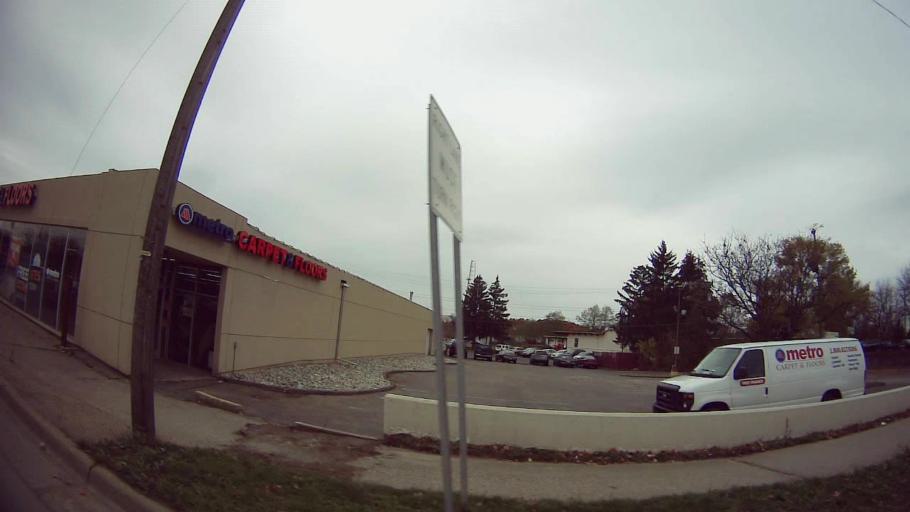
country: US
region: Michigan
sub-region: Oakland County
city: Pontiac
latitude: 42.6668
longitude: -83.3307
